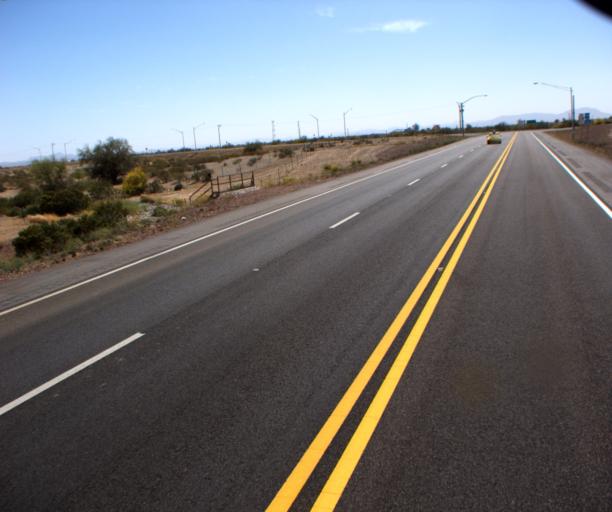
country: US
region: Arizona
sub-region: Maricopa County
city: Gila Bend
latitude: 32.9554
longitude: -112.6848
